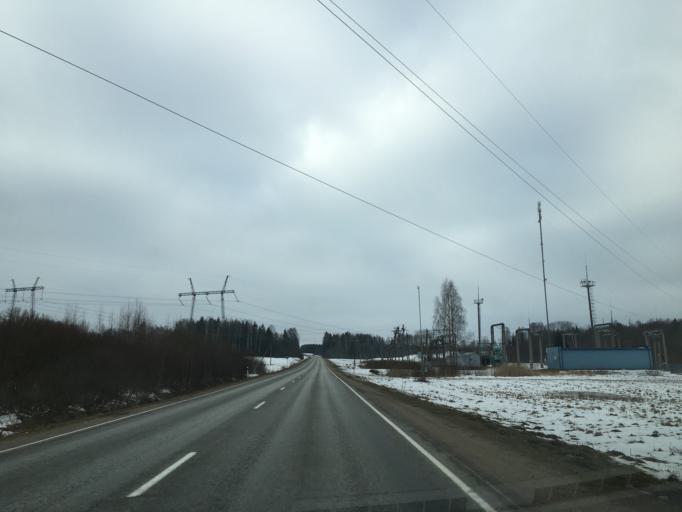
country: EE
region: Tartu
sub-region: Elva linn
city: Elva
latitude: 58.1363
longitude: 26.2463
